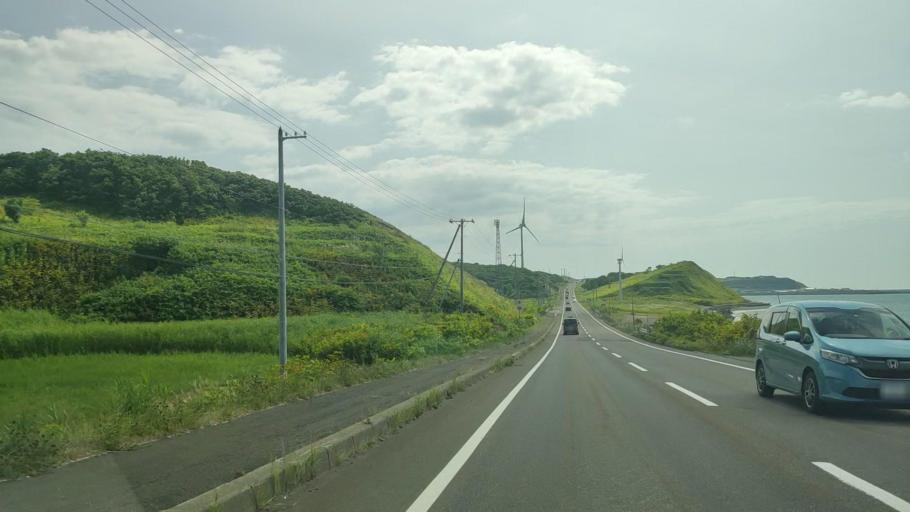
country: JP
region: Hokkaido
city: Rumoi
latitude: 44.3241
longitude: 141.6729
